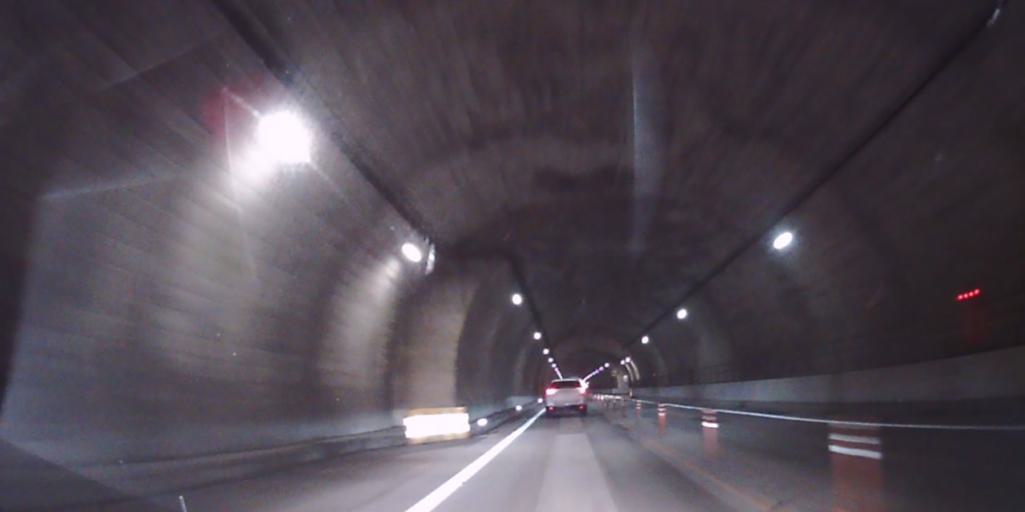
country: JP
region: Hokkaido
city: Date
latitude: 42.5744
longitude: 140.7410
